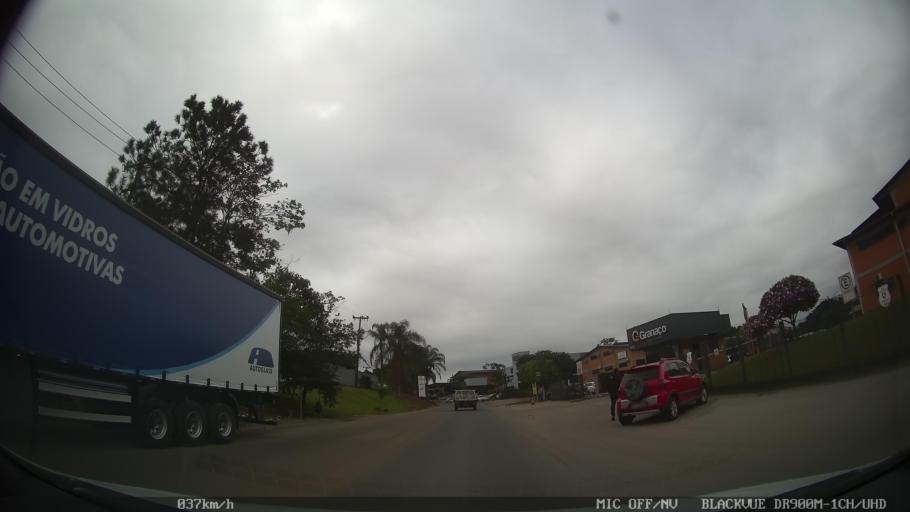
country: BR
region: Santa Catarina
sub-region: Joinville
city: Joinville
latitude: -26.2603
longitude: -48.8834
